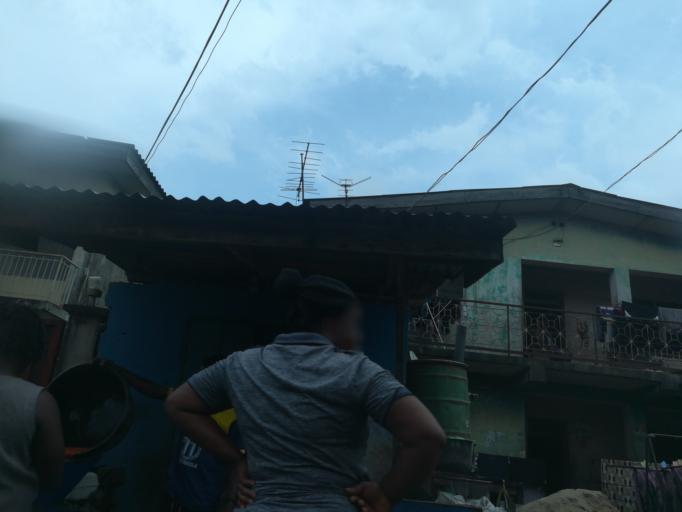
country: NG
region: Lagos
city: Oshodi
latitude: 6.5771
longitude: 3.3410
